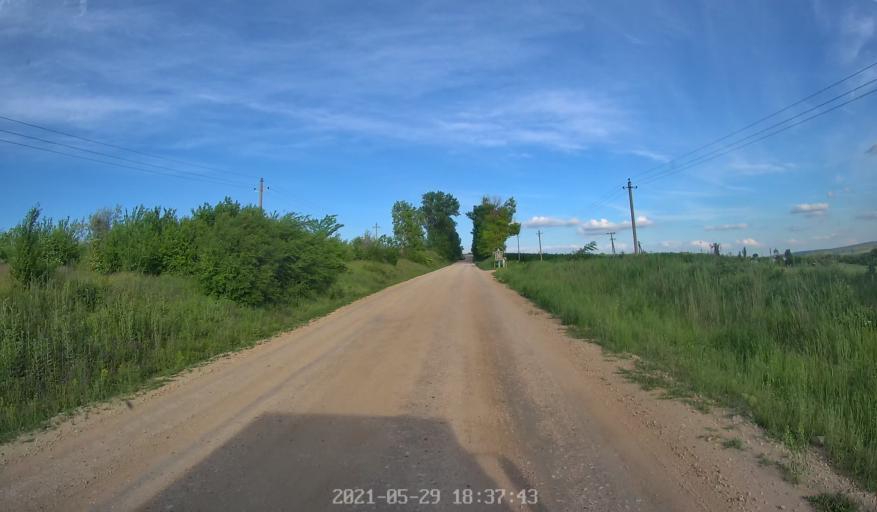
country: MD
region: Chisinau
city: Singera
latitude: 46.8035
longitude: 28.9328
